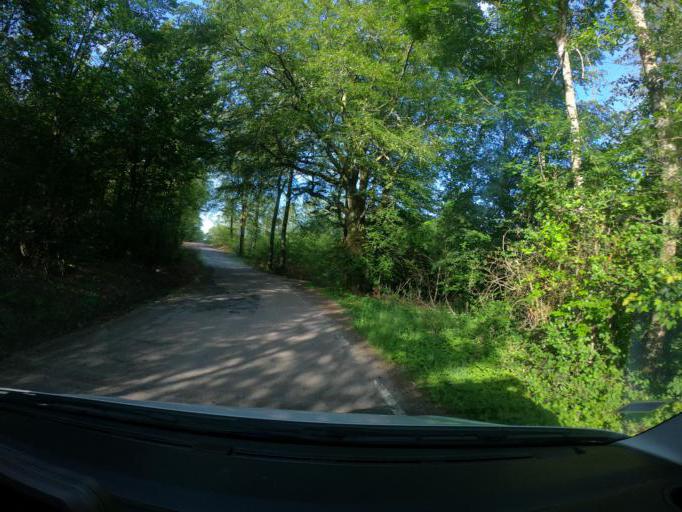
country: SE
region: Skane
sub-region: Orkelljunga Kommun
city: OErkelljunga
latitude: 56.3430
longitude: 13.1213
